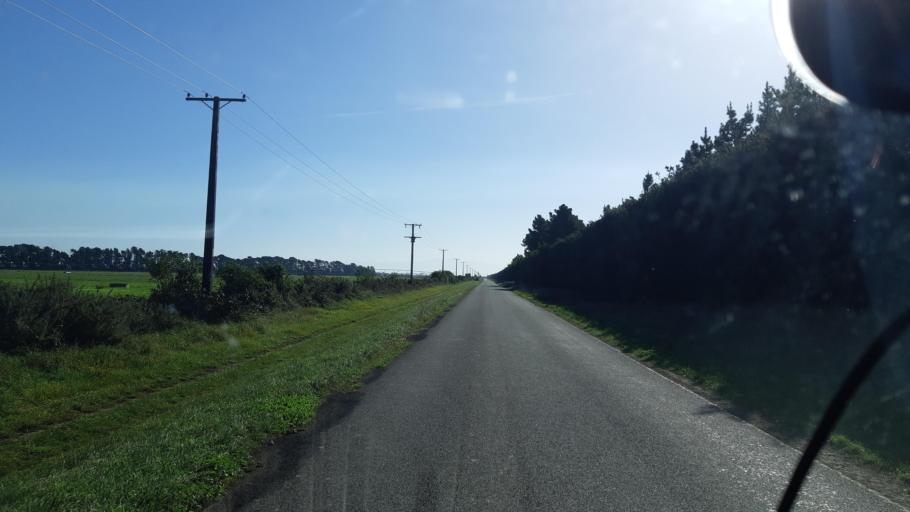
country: NZ
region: Canterbury
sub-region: Selwyn District
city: Burnham
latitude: -43.6381
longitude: 172.2363
